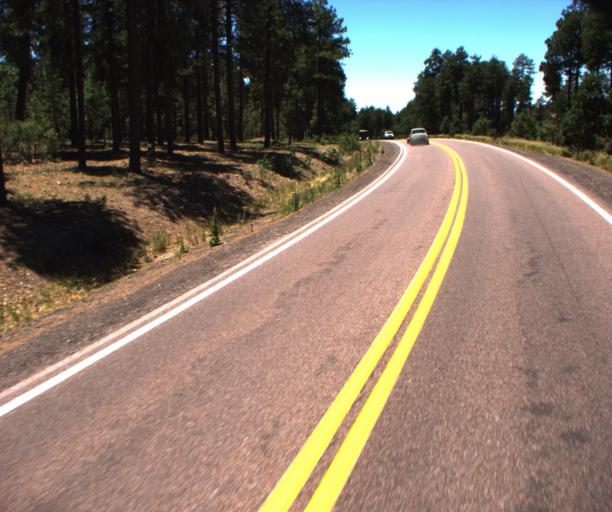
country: US
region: Arizona
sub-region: Gila County
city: Pine
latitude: 34.4434
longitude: -111.4651
